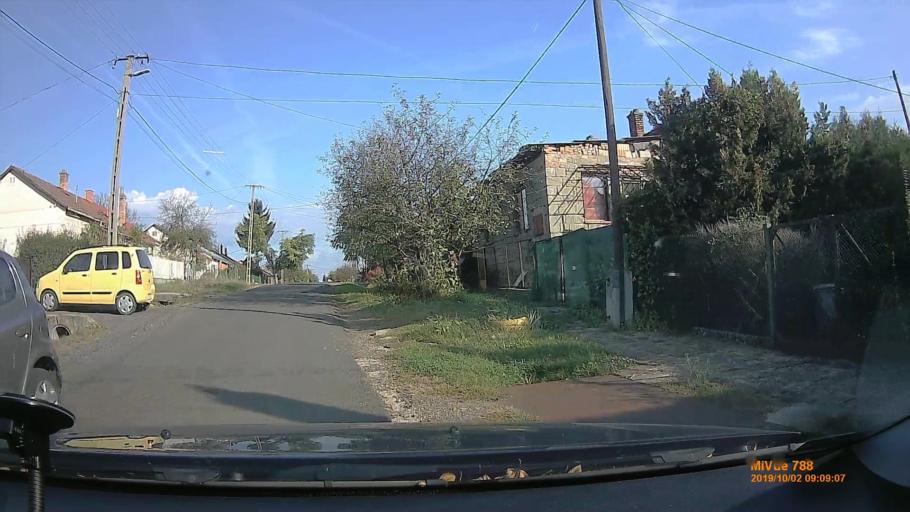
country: HU
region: Nograd
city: Batonyterenye
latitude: 48.0149
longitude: 19.8211
